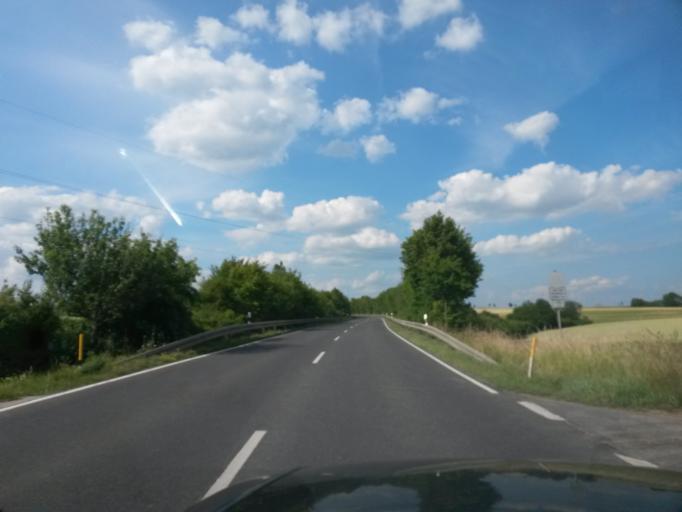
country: DE
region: Bavaria
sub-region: Regierungsbezirk Unterfranken
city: Estenfeld
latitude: 49.8313
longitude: 9.9880
